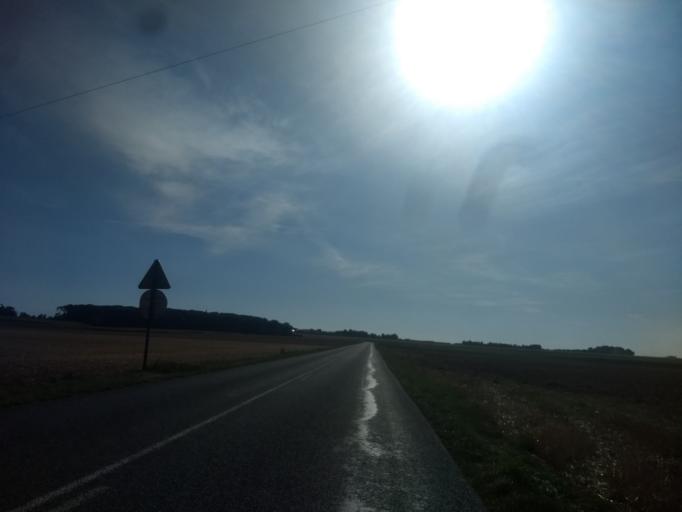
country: FR
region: Nord-Pas-de-Calais
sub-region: Departement du Pas-de-Calais
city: Roeux
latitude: 50.2830
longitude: 2.9004
